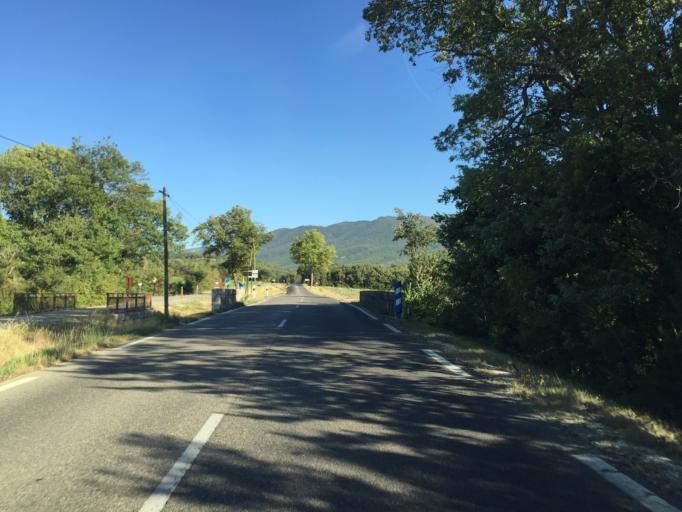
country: FR
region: Provence-Alpes-Cote d'Azur
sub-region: Departement du Vaucluse
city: Saignon
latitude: 43.8639
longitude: 5.4640
